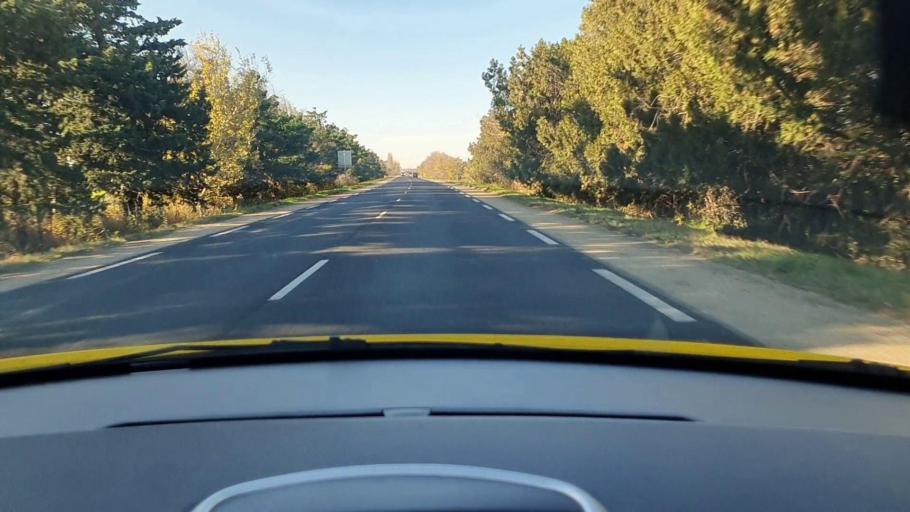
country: FR
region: Languedoc-Roussillon
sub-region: Departement du Gard
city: Fourques
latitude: 43.7031
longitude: 4.5691
